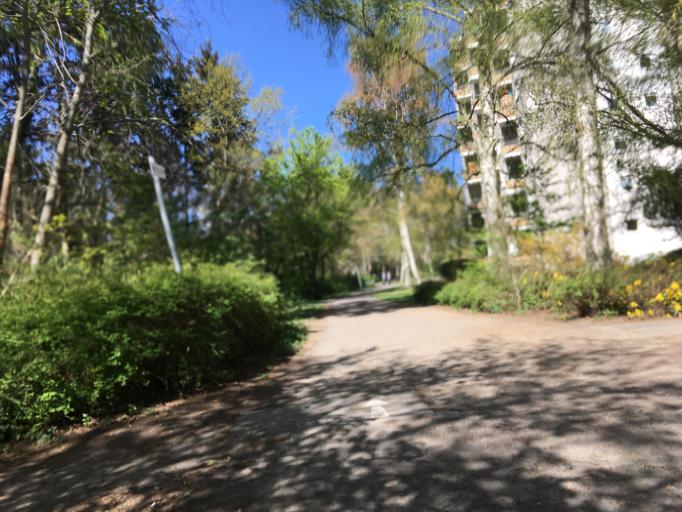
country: DE
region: Berlin
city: Reinickendorf
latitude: 52.5692
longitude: 13.3419
